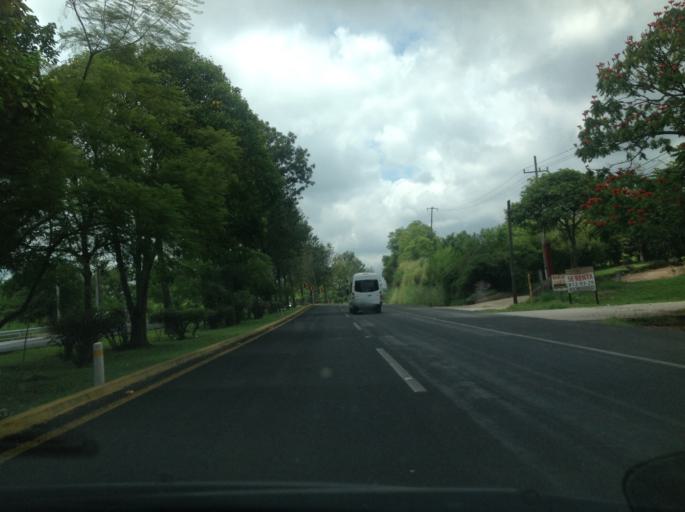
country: MX
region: Veracruz
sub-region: Emiliano Zapata
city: Jacarandas
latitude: 19.5043
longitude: -96.8496
